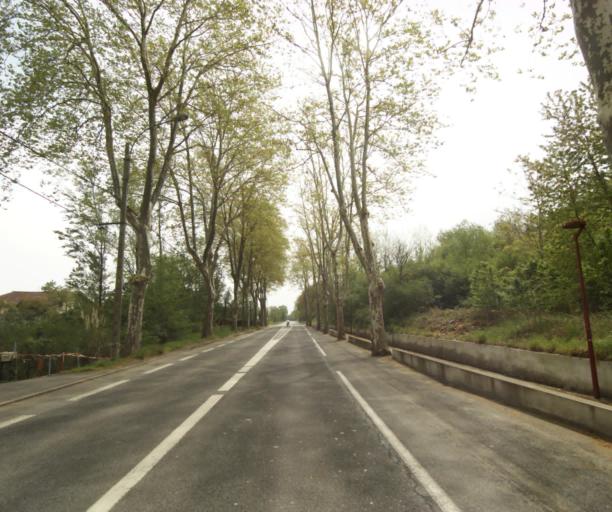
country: FR
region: Midi-Pyrenees
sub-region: Departement de la Haute-Garonne
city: Pechabou
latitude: 43.5068
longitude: 1.5070
